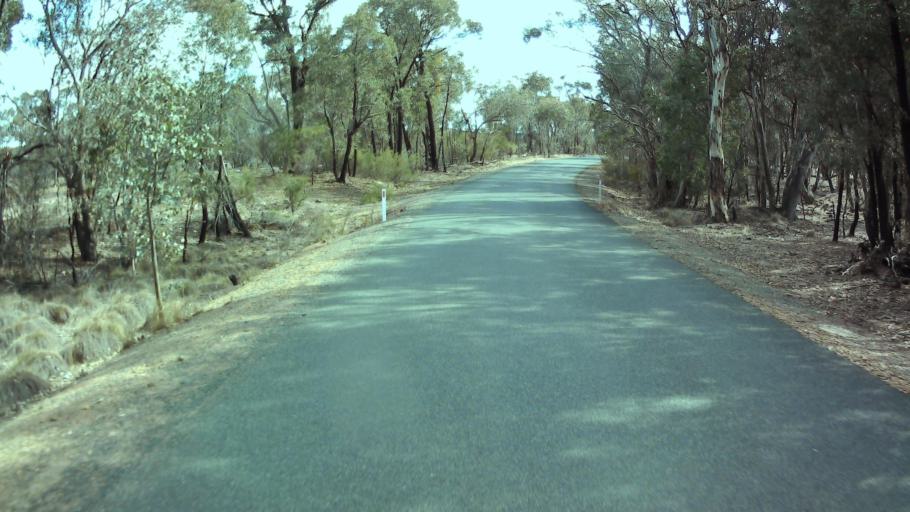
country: AU
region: New South Wales
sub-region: Weddin
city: Grenfell
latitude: -33.8724
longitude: 148.2023
